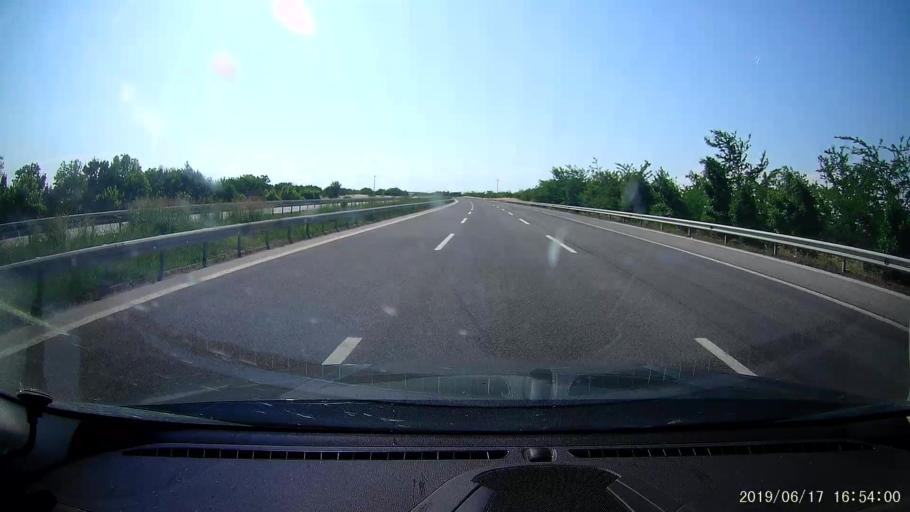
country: TR
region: Kirklareli
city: Inece
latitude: 41.5705
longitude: 27.0087
